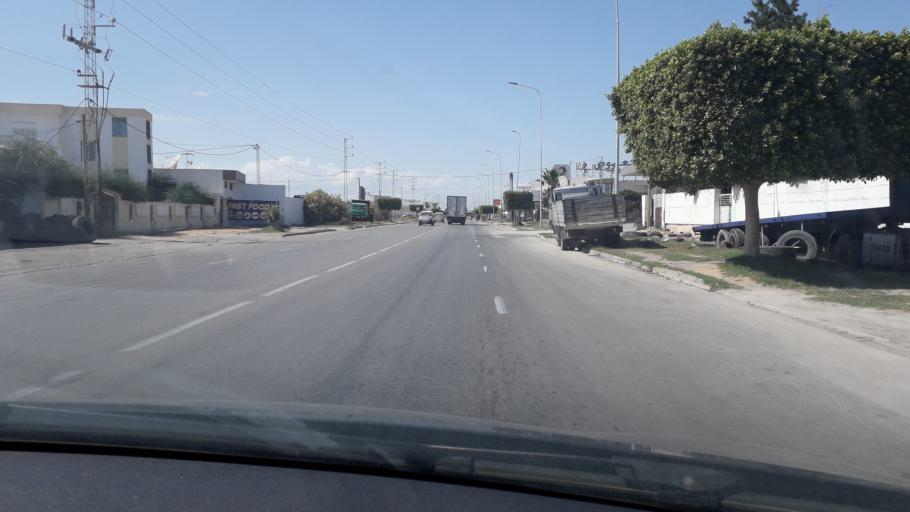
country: TN
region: Safaqis
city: Al Qarmadah
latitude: 34.8383
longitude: 10.7647
